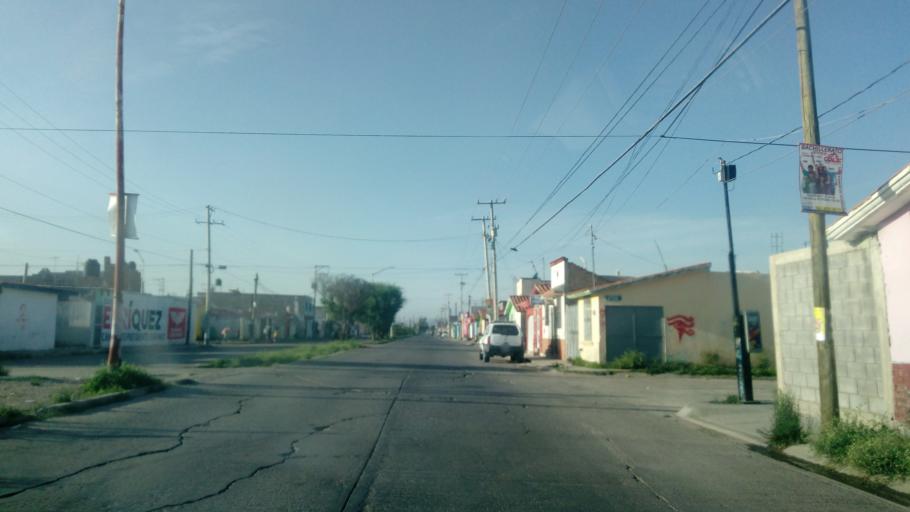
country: MX
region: Durango
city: Victoria de Durango
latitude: 24.0648
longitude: -104.5858
